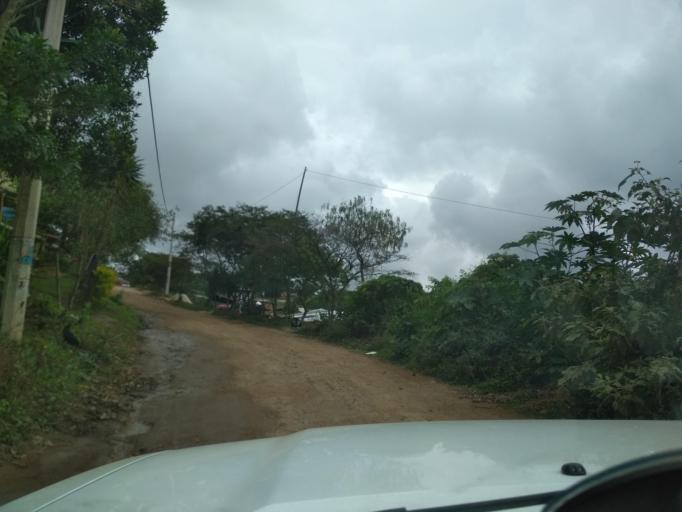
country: MX
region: Veracruz
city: El Castillo
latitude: 19.5473
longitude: -96.8512
